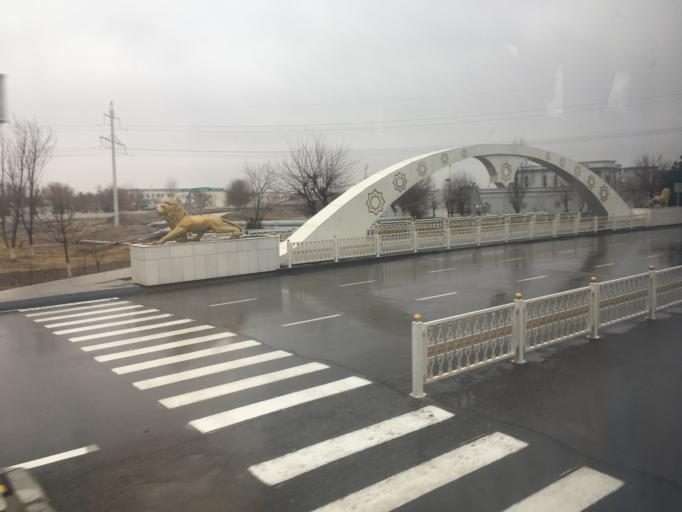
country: TM
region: Lebap
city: Turkmenabat
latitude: 39.0963
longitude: 63.5859
